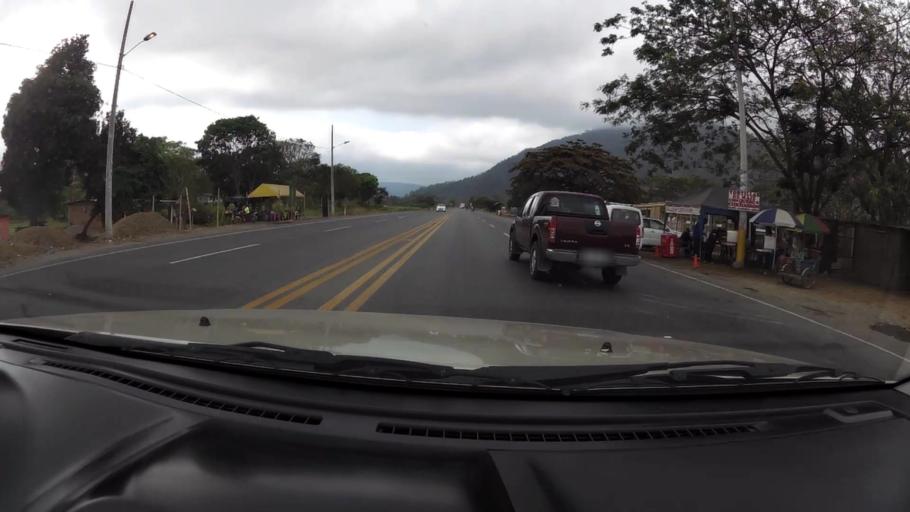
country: EC
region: Guayas
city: Coronel Marcelino Mariduena
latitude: -2.3847
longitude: -79.6311
